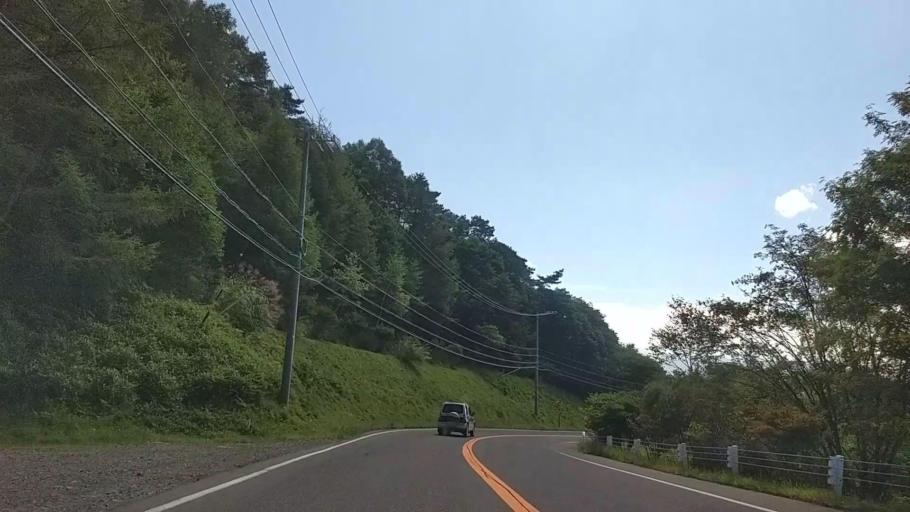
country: JP
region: Nagano
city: Chino
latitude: 36.0866
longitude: 138.2230
